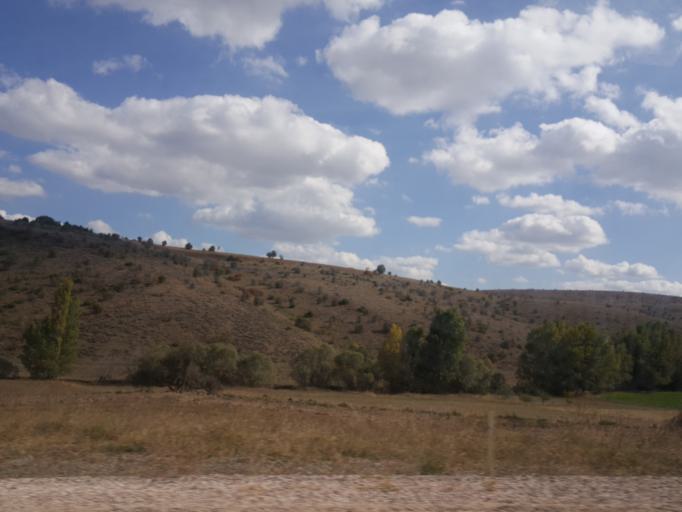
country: TR
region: Tokat
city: Camlibel
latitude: 40.1574
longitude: 36.4039
